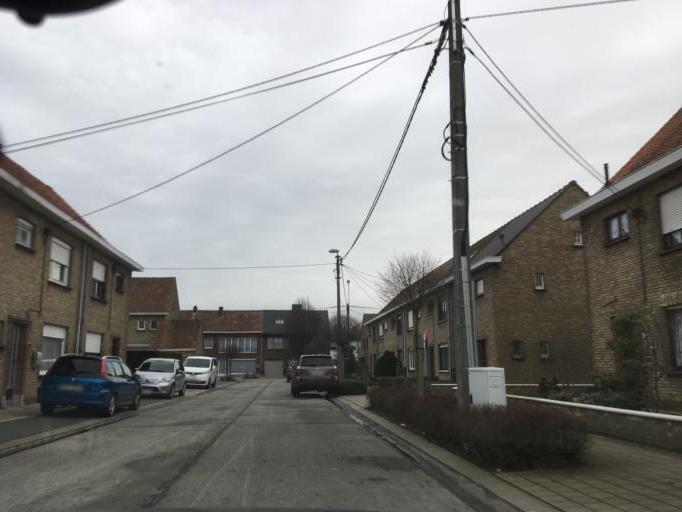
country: BE
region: Flanders
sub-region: Provincie West-Vlaanderen
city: Roeselare
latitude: 50.9521
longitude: 3.1082
